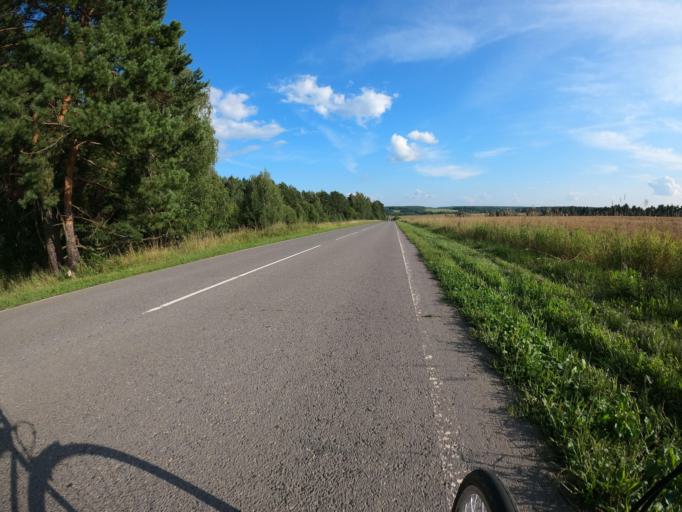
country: RU
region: Moskovskaya
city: Meshcherino
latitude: 55.1530
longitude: 38.4324
